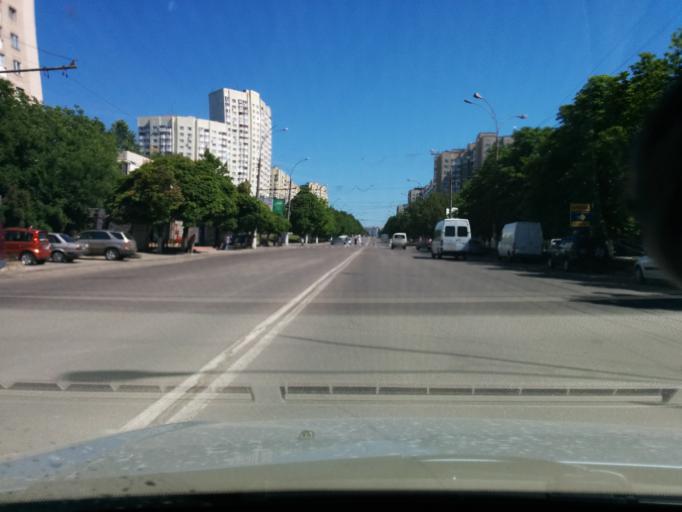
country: MD
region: Chisinau
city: Chisinau
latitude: 47.0485
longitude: 28.8631
